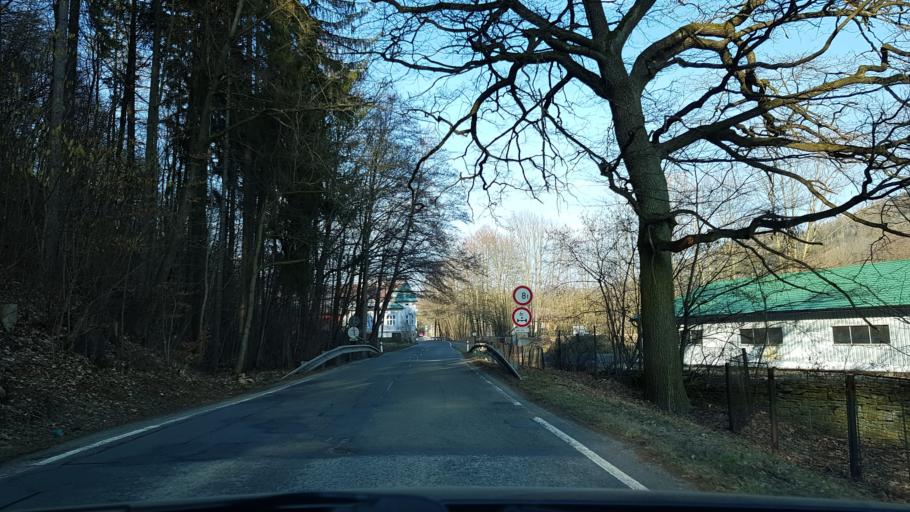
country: CZ
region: Olomoucky
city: Dolni Bohdikov
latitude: 50.0253
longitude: 16.8974
